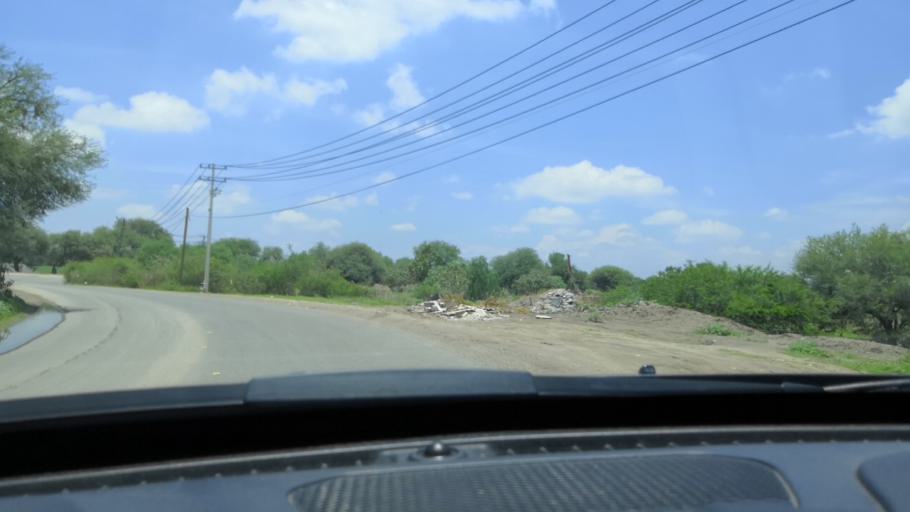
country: MX
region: Guanajuato
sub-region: Leon
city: Ladrilleras del Refugio
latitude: 21.0565
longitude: -101.5600
